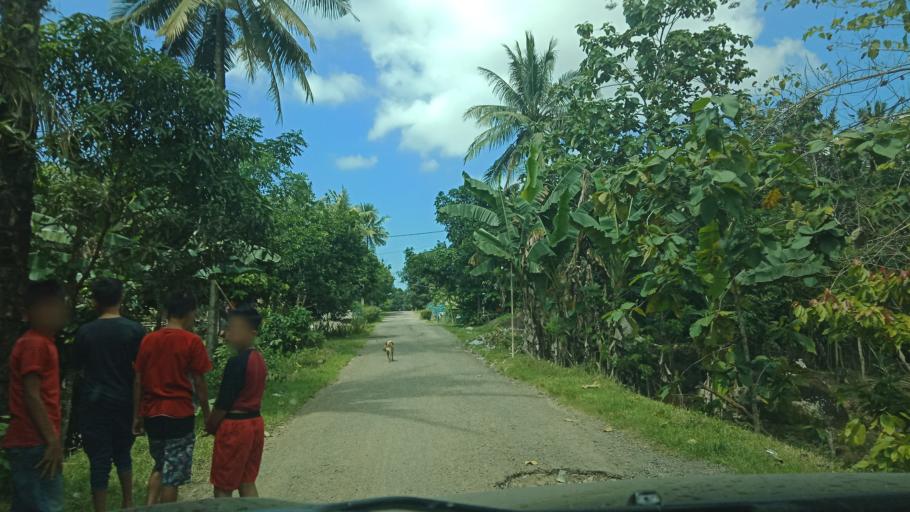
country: ID
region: South Sulawesi
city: Kadai
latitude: -4.7724
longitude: 120.3360
